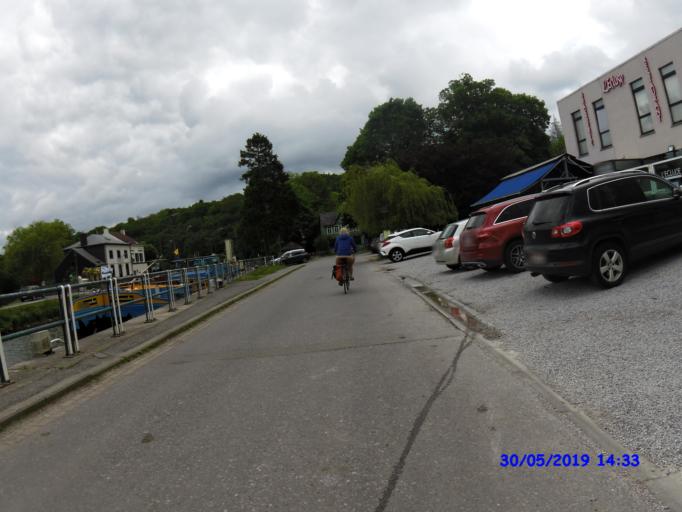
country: BE
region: Wallonia
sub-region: Province du Hainaut
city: Thuin
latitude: 50.3670
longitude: 4.3342
